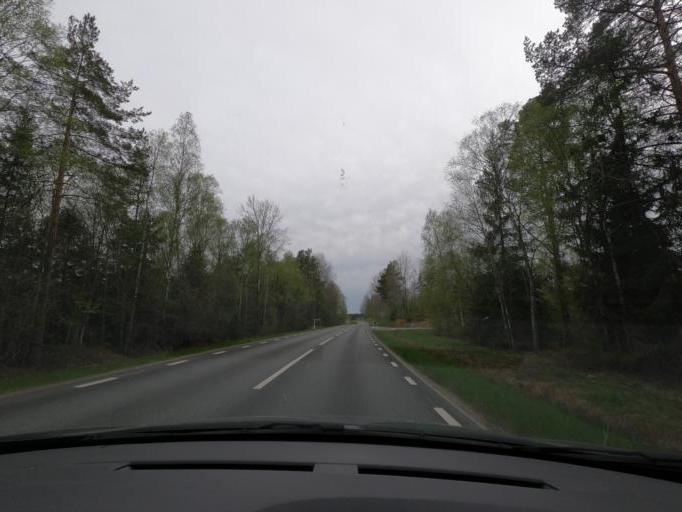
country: SE
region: Joenkoeping
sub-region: Varnamo Kommun
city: Bredaryd
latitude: 57.2066
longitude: 13.7650
